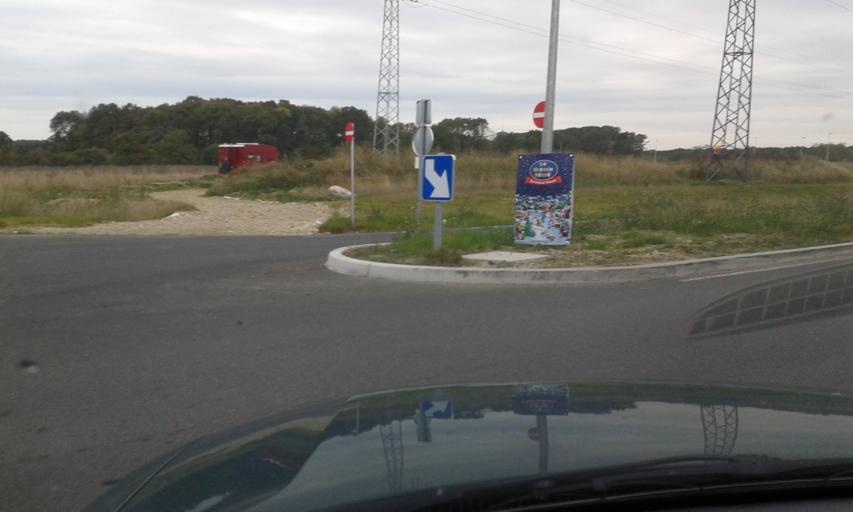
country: FR
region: Centre
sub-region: Departement du Loiret
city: Saran
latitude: 47.9619
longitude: 1.8843
